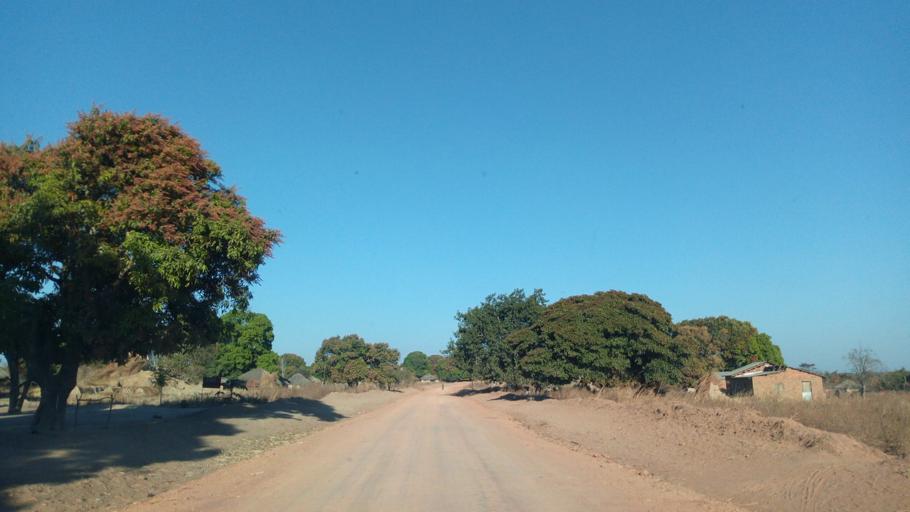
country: ZM
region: Luapula
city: Mwense
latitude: -10.4442
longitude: 28.5785
